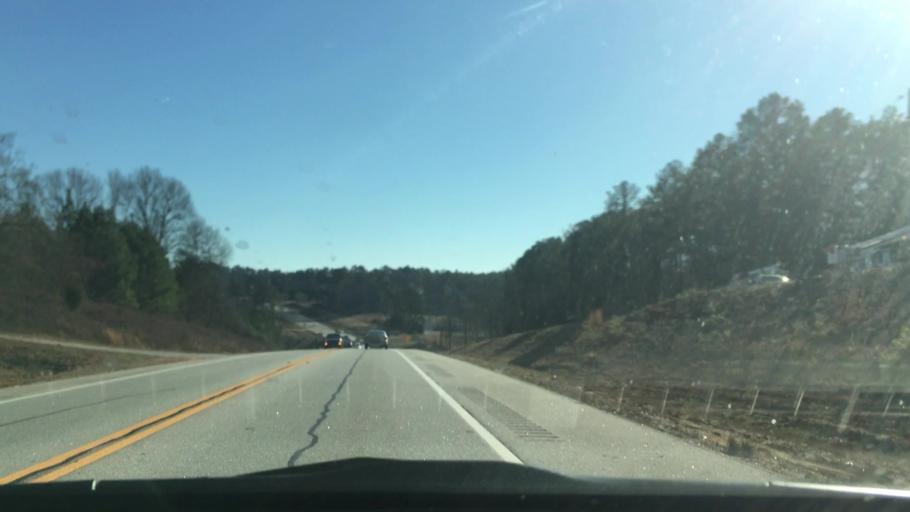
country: US
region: Georgia
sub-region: Henry County
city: McDonough
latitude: 33.5286
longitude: -84.1397
